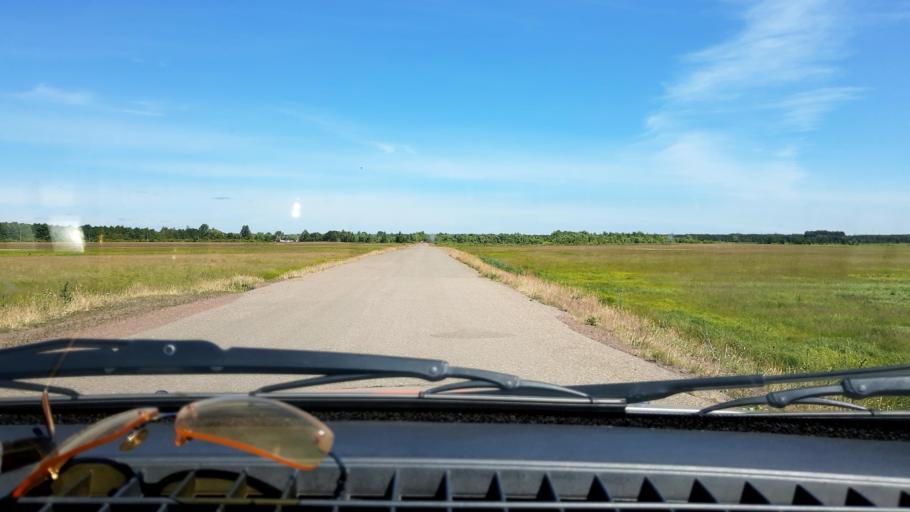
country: RU
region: Bashkortostan
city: Mikhaylovka
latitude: 54.9647
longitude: 55.8021
